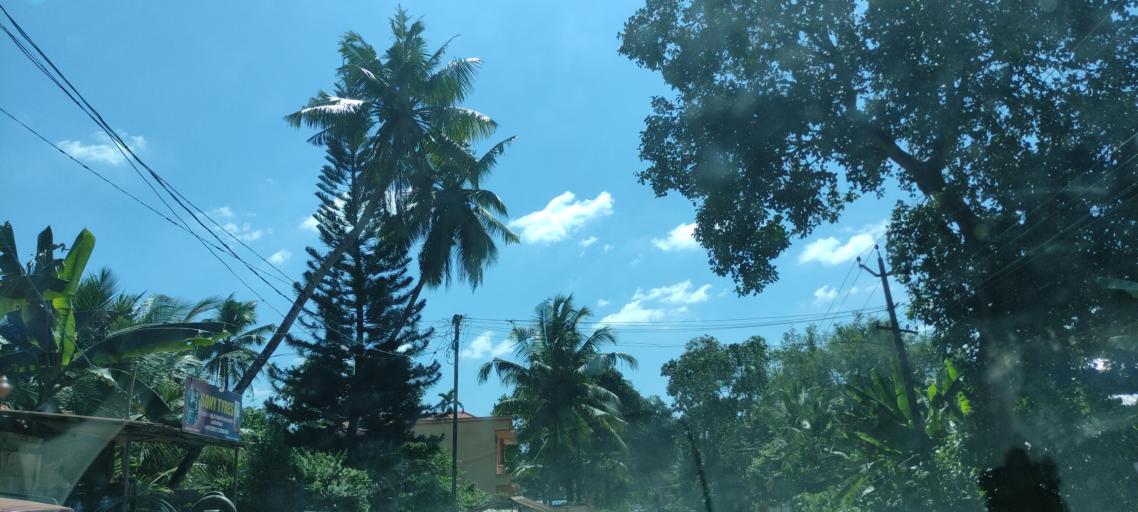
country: IN
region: Kerala
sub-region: Pattanamtitta
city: Adur
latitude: 9.1000
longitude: 76.6889
